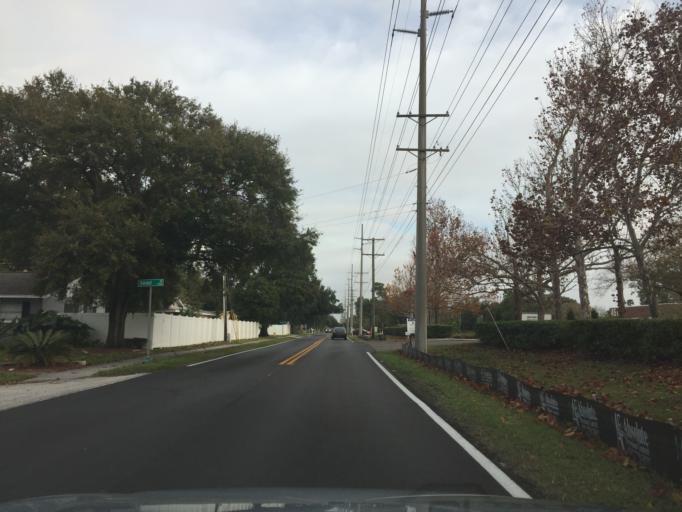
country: US
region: Florida
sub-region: Hillsborough County
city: Town 'n' Country
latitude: 27.9844
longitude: -82.5505
